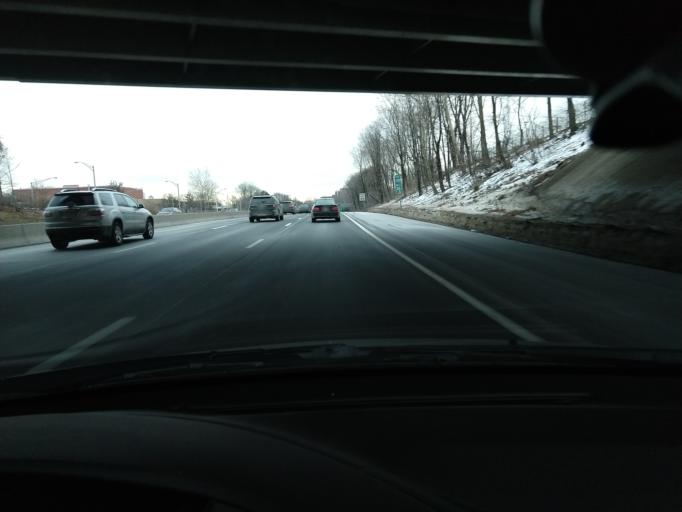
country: US
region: New Jersey
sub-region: Essex County
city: Orange
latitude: 40.7693
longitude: -74.2296
